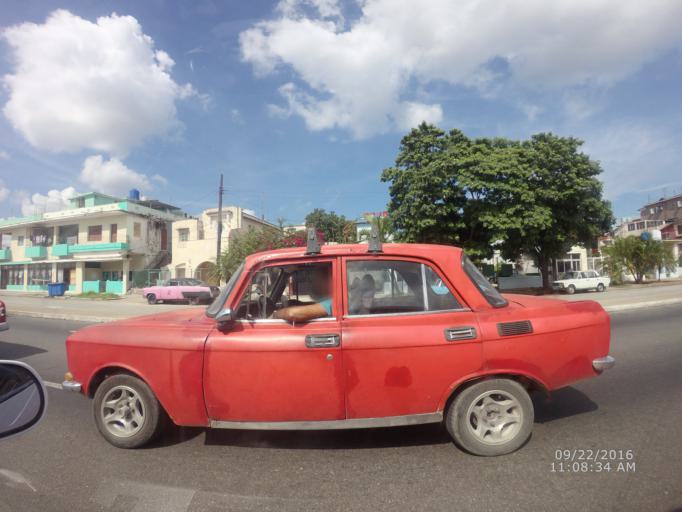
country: CU
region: La Habana
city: Cerro
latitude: 23.1124
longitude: -82.4180
